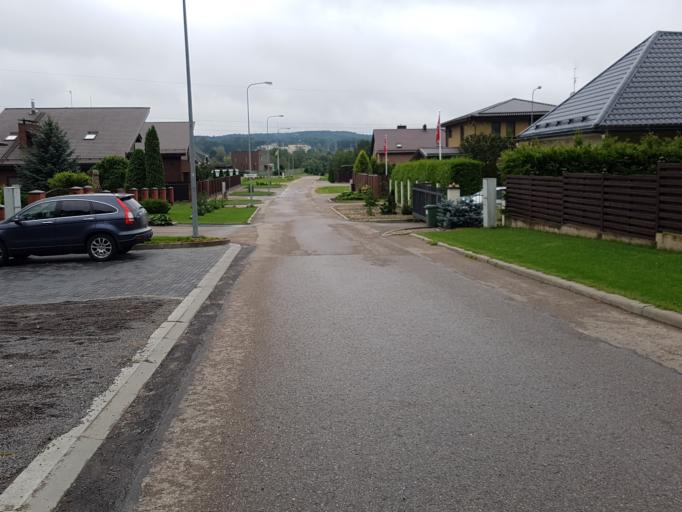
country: LT
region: Vilnius County
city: Lazdynai
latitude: 54.6536
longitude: 25.2079
